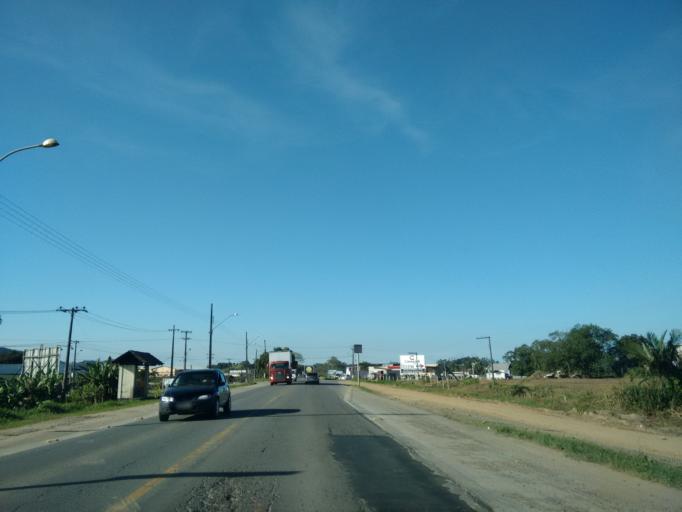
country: BR
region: Santa Catarina
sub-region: Guaramirim
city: Guaramirim
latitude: -26.4718
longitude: -48.9725
